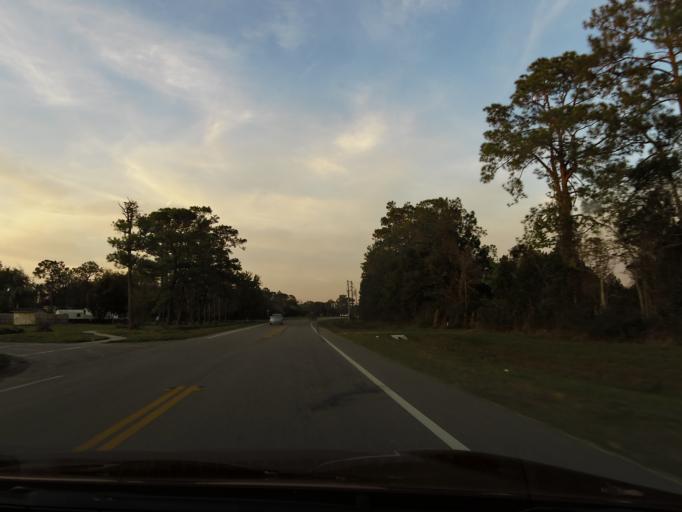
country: US
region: Florida
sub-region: Volusia County
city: North DeLand
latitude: 29.0816
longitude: -81.3049
